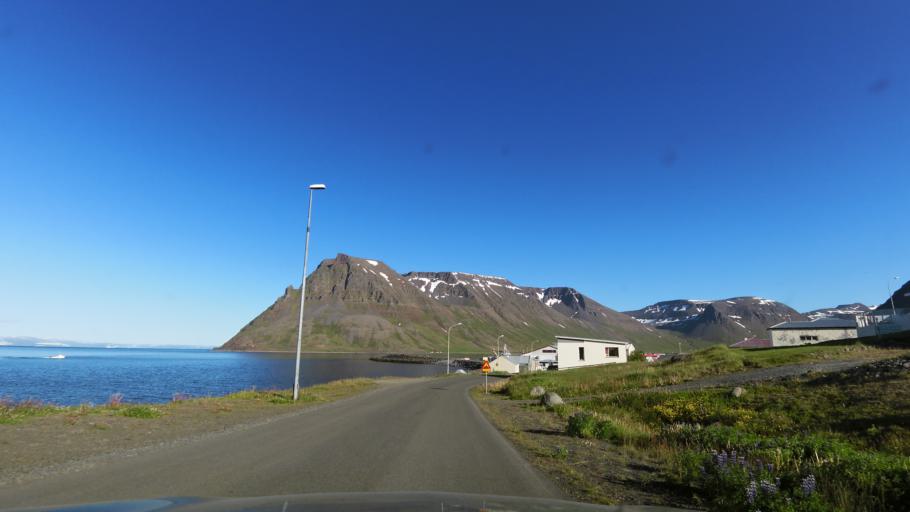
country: IS
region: Westfjords
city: Isafjoerdur
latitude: 66.1621
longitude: -23.2486
